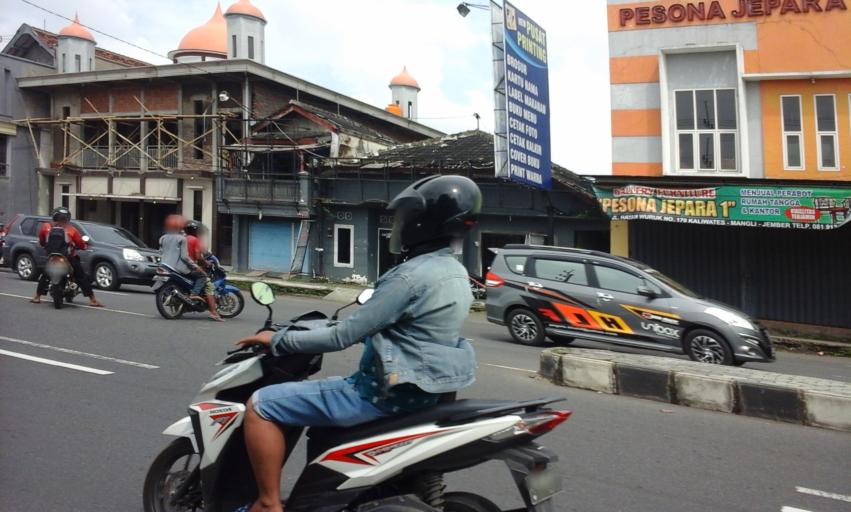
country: ID
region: East Java
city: Mangli
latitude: -8.1889
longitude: 113.6551
